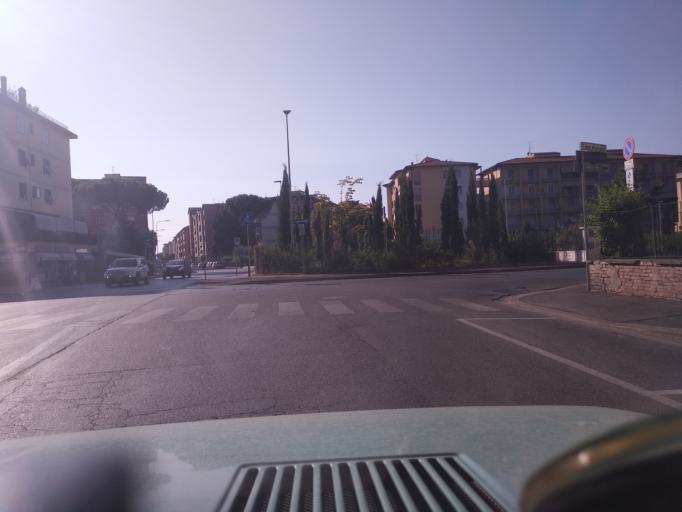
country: IT
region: Tuscany
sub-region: Province of Florence
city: Florence
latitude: 43.7780
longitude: 11.2130
